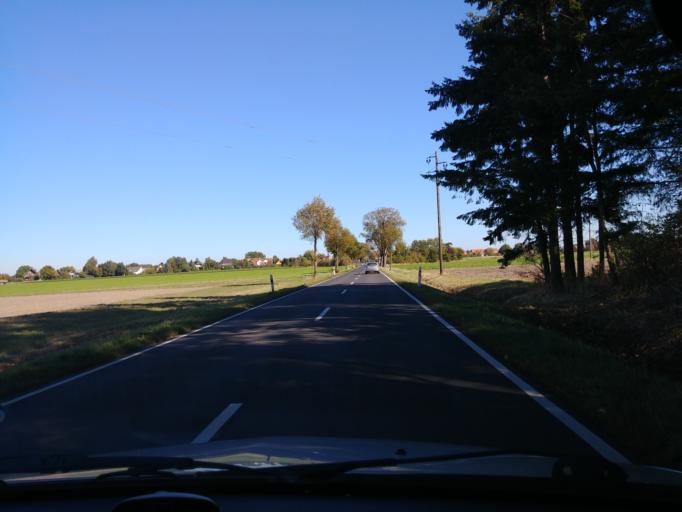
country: DE
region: Lower Saxony
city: Leiferde
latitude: 52.4296
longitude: 10.4311
